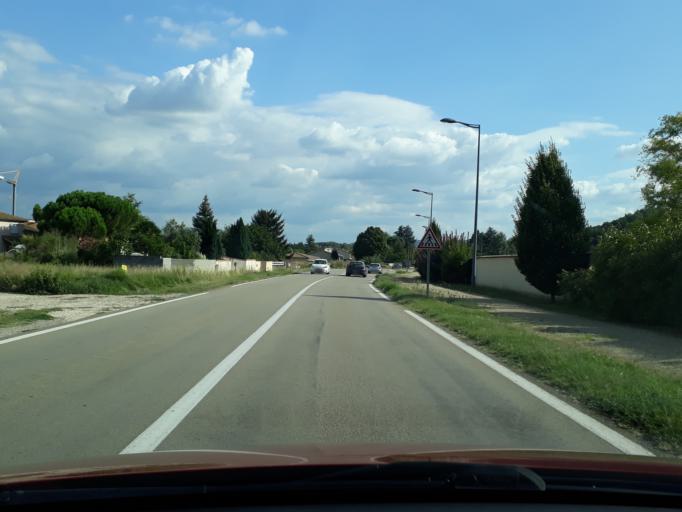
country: FR
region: Rhone-Alpes
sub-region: Departement de la Loire
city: Saint-Pierre-de-Boeuf
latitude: 45.3607
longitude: 4.7554
